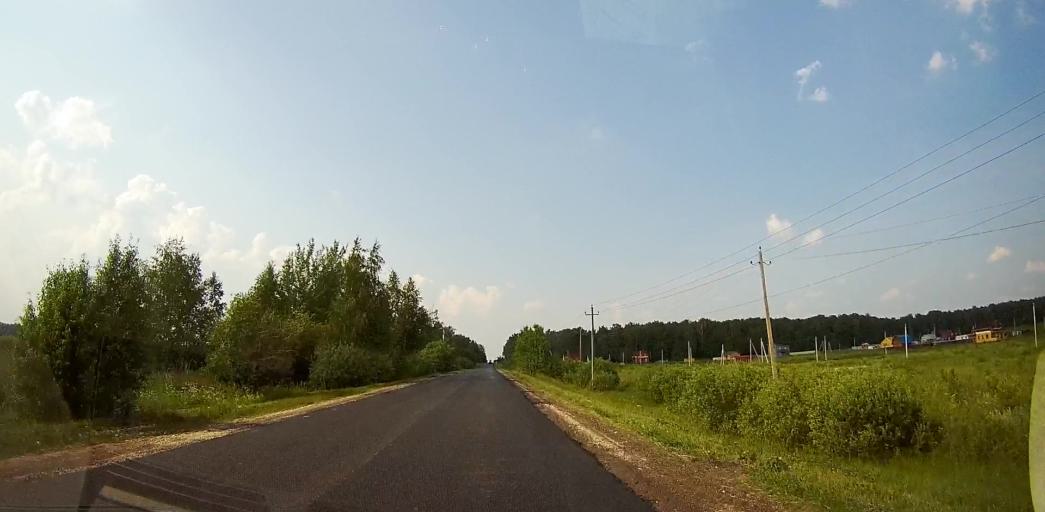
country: RU
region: Moskovskaya
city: Il'inskoye
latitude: 55.2299
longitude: 37.9233
